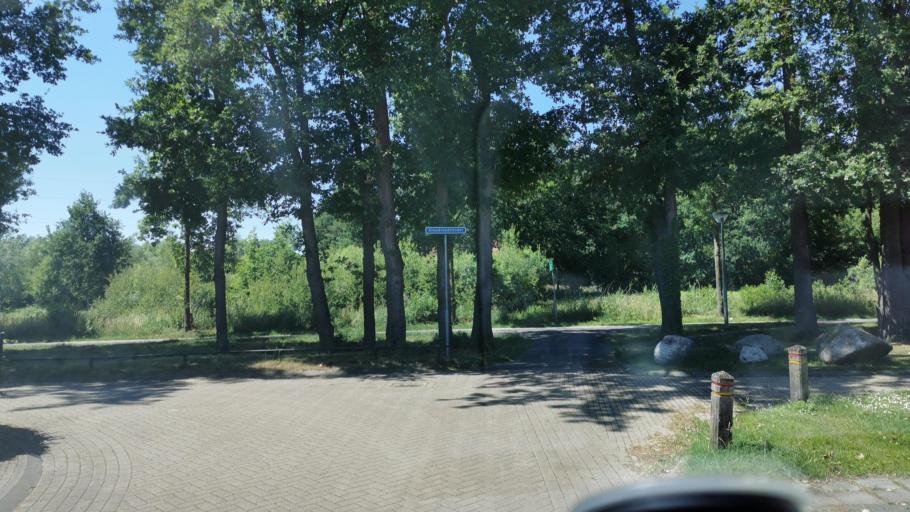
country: NL
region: Overijssel
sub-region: Gemeente Enschede
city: Enschede
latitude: 52.2131
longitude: 6.9570
